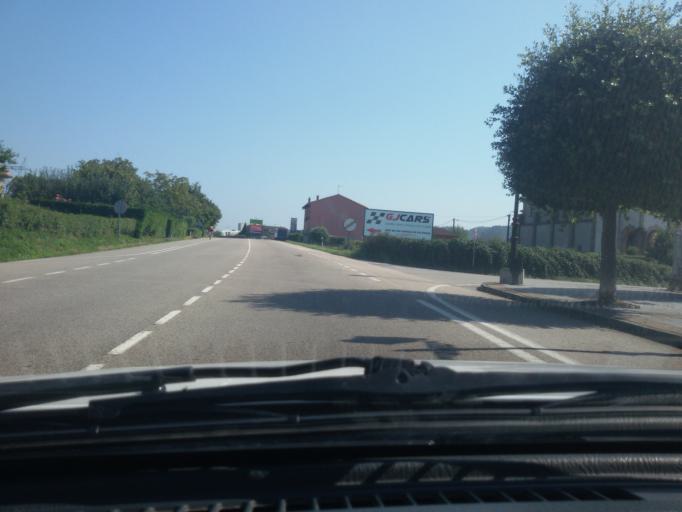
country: ES
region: Asturias
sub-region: Province of Asturias
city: Norena
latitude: 43.3854
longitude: -5.6955
